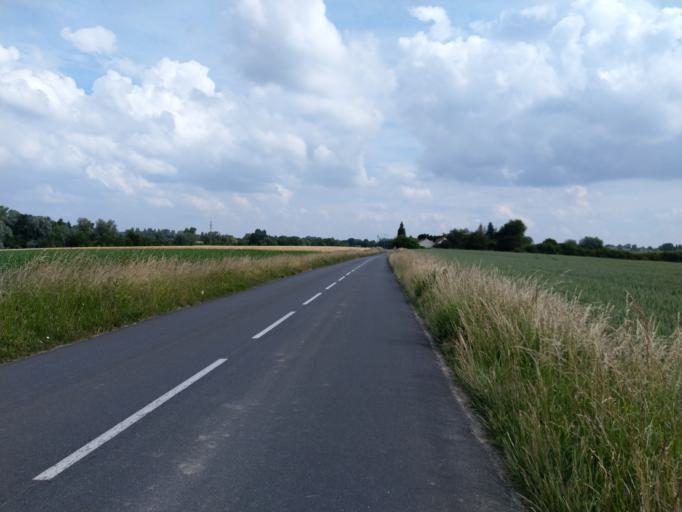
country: FR
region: Nord-Pas-de-Calais
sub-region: Departement du Nord
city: Rousies
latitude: 50.3085
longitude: 3.9981
